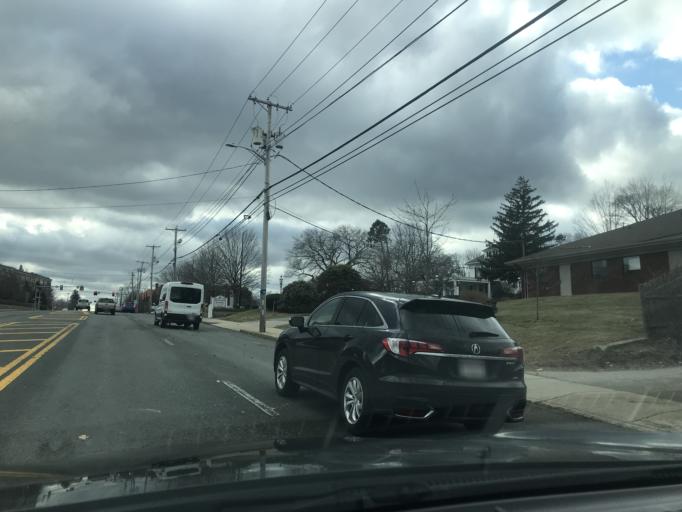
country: US
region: Massachusetts
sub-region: Norfolk County
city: Weymouth
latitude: 42.1784
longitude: -70.9554
